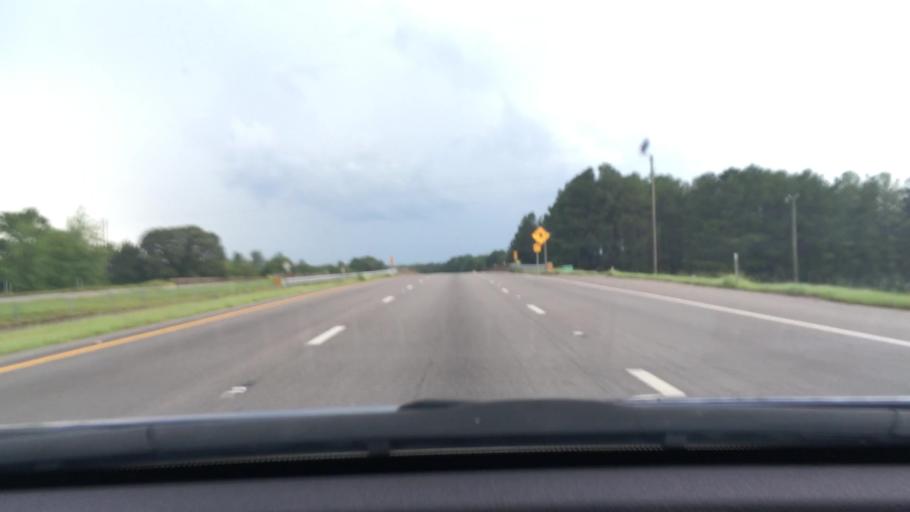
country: US
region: South Carolina
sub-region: Kershaw County
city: Lugoff
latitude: 34.1897
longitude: -80.6865
